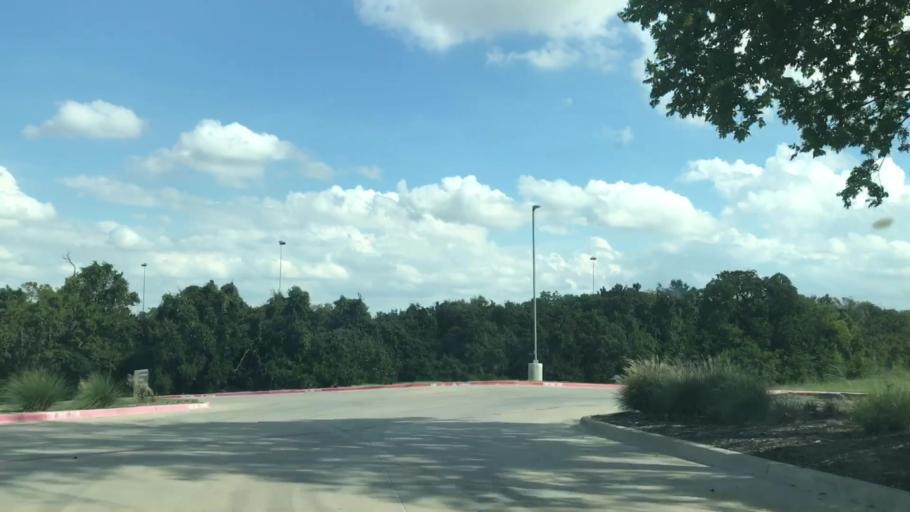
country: US
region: Texas
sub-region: Dallas County
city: Coppell
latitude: 32.9791
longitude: -97.0286
